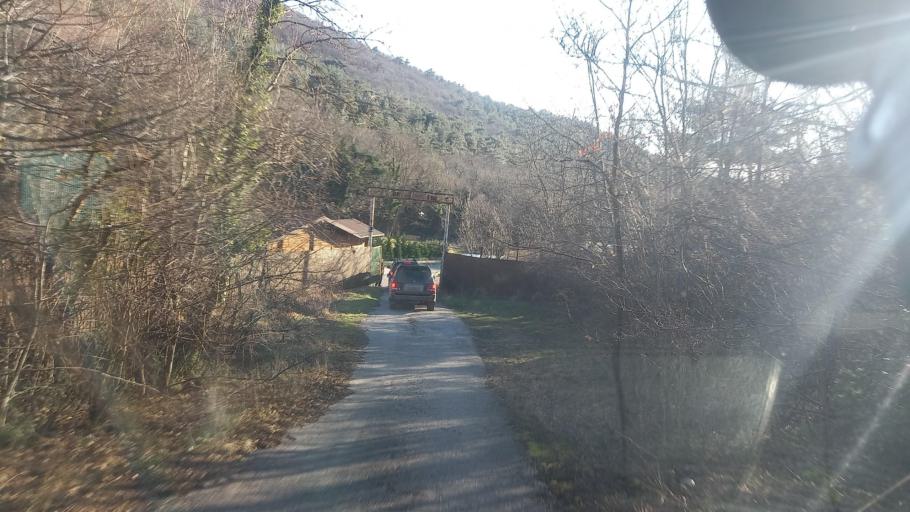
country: RU
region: Krasnodarskiy
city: Kabardinka
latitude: 44.6096
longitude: 37.9415
